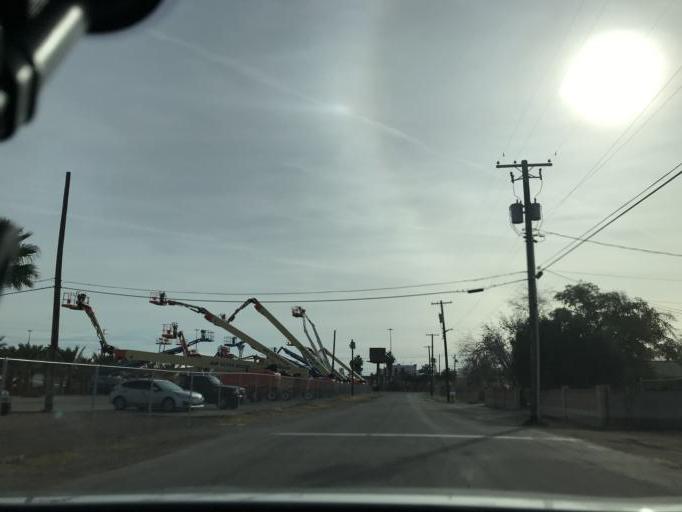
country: US
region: Nevada
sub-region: Clark County
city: Las Vegas
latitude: 36.1787
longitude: -115.1671
